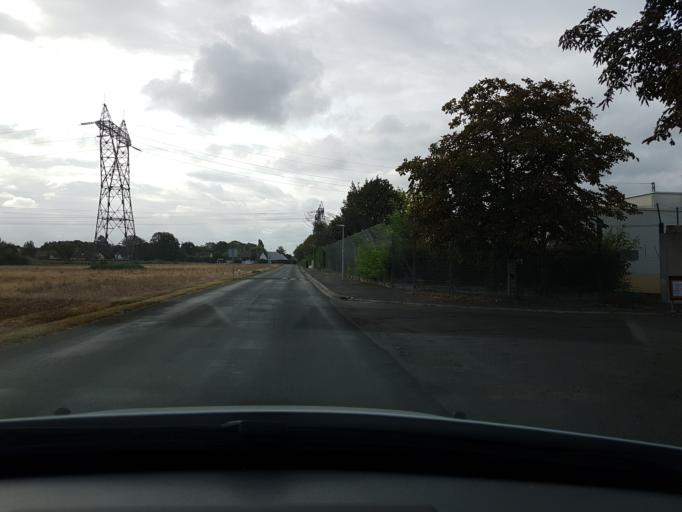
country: FR
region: Centre
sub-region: Departement d'Indre-et-Loire
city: Larcay
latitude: 47.3532
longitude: 0.7676
